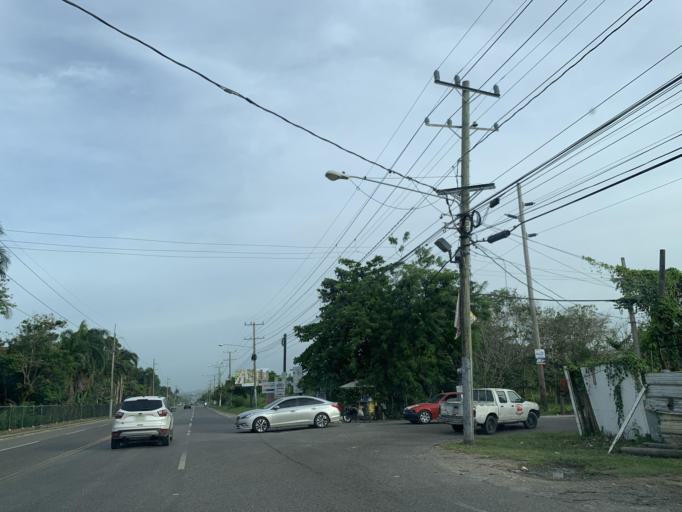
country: DO
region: Puerto Plata
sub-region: Puerto Plata
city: Puerto Plata
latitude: 19.7627
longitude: -70.6482
